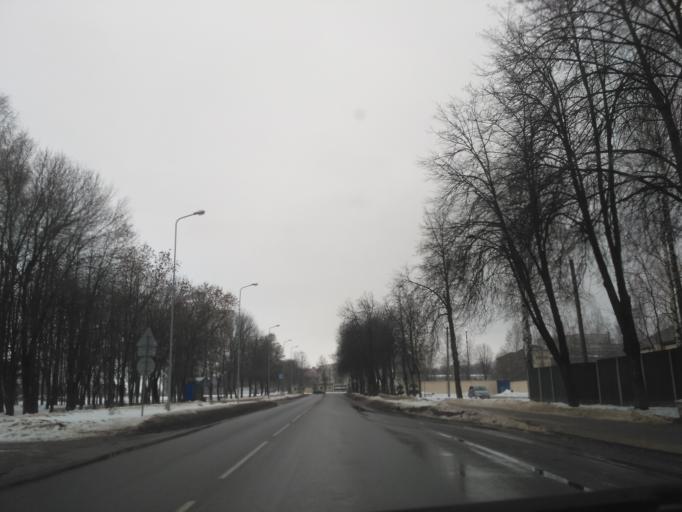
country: BY
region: Minsk
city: Horad Zhodzina
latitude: 54.0945
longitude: 28.3334
